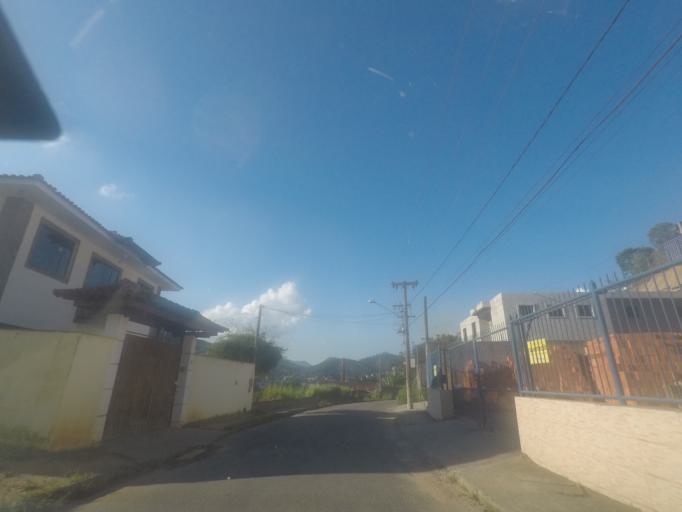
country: BR
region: Rio de Janeiro
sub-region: Petropolis
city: Petropolis
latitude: -22.4913
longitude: -43.1509
